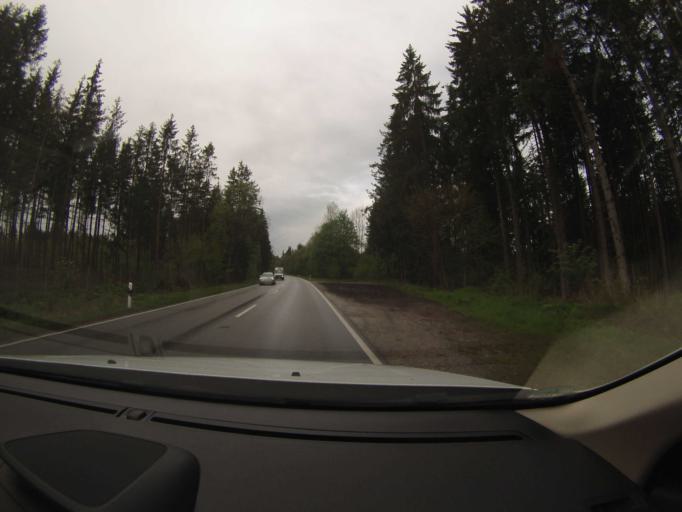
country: DE
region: Bavaria
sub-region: Upper Bavaria
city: Oberhaching
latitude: 48.0120
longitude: 11.6373
